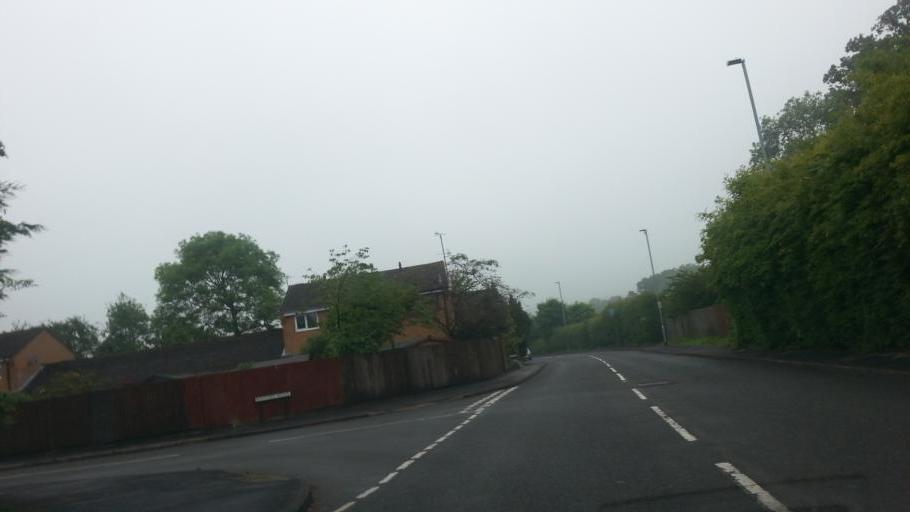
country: GB
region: England
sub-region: Leicestershire
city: Oadby
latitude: 52.5922
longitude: -1.0606
